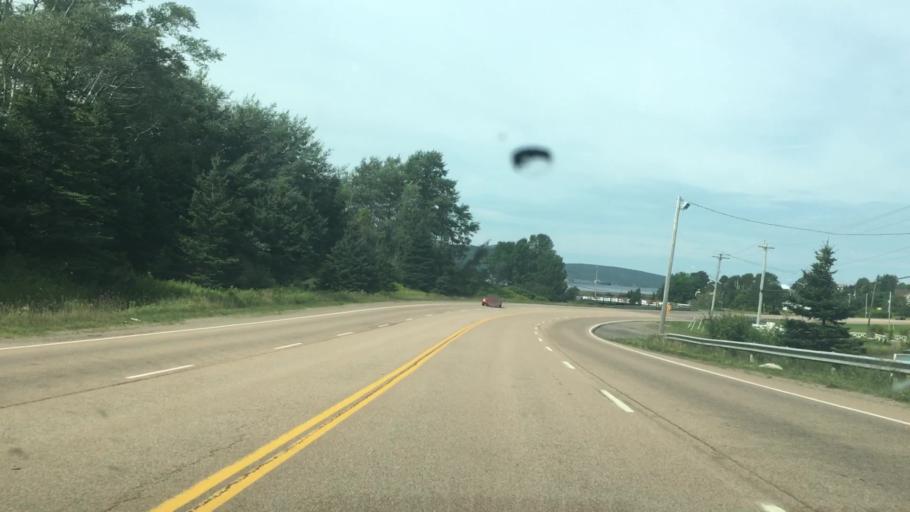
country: CA
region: Nova Scotia
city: Port Hawkesbury
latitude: 45.6211
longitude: -61.3621
